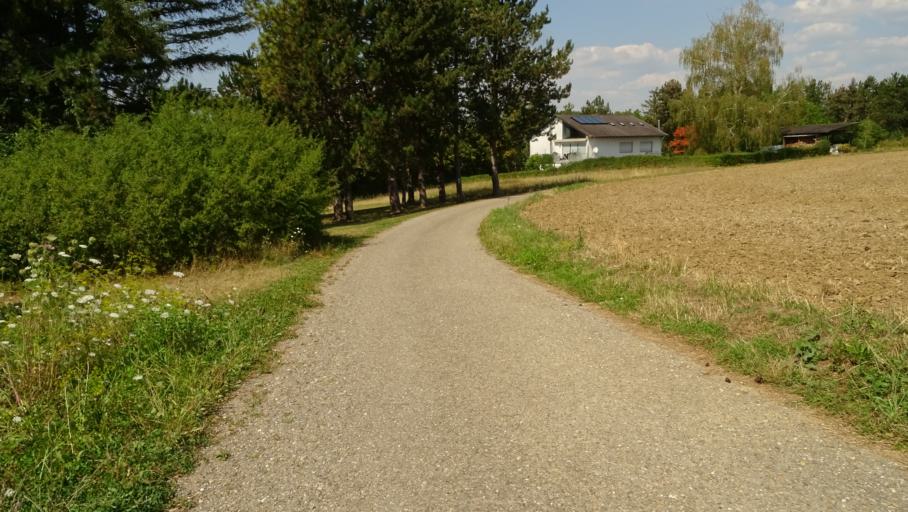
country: DE
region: Baden-Wuerttemberg
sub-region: Karlsruhe Region
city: Obrigheim
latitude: 49.3539
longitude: 9.1170
